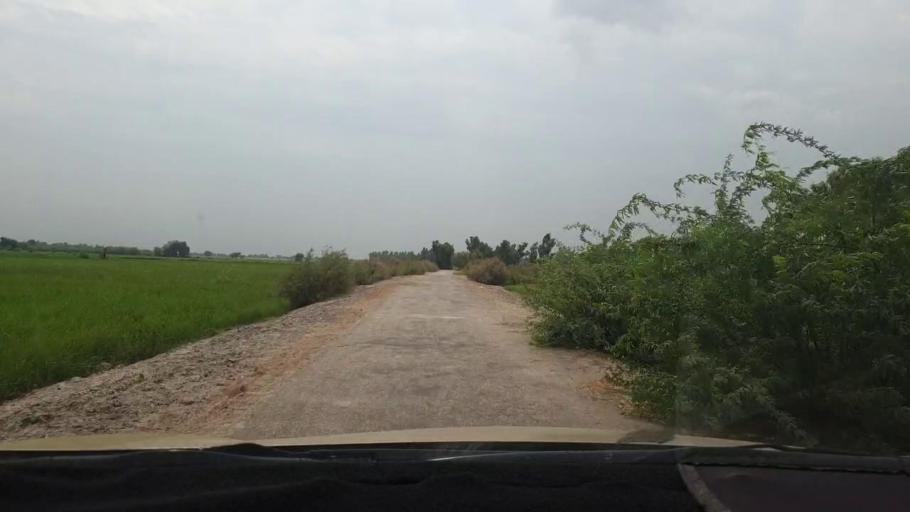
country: PK
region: Sindh
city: Naudero
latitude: 27.6259
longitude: 68.3220
